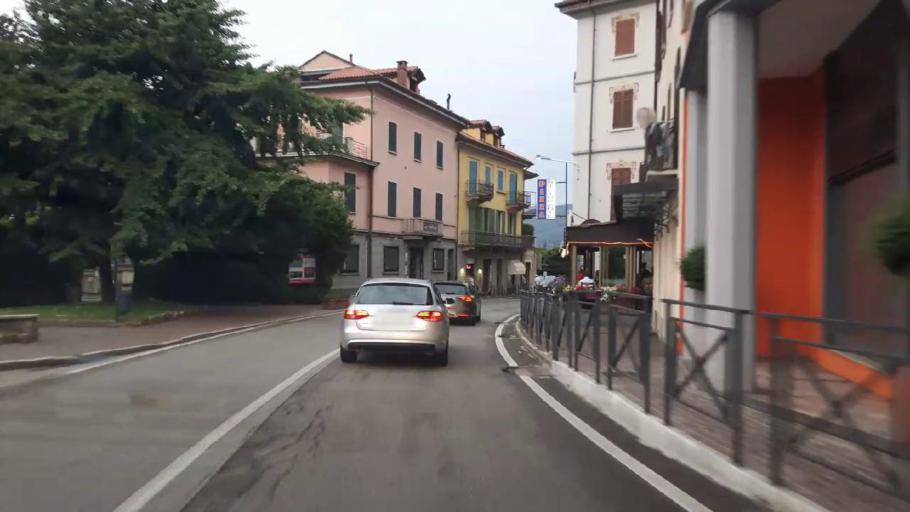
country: IT
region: Piedmont
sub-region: Provincia Verbano-Cusio-Ossola
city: Baveno
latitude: 45.9100
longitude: 8.5052
